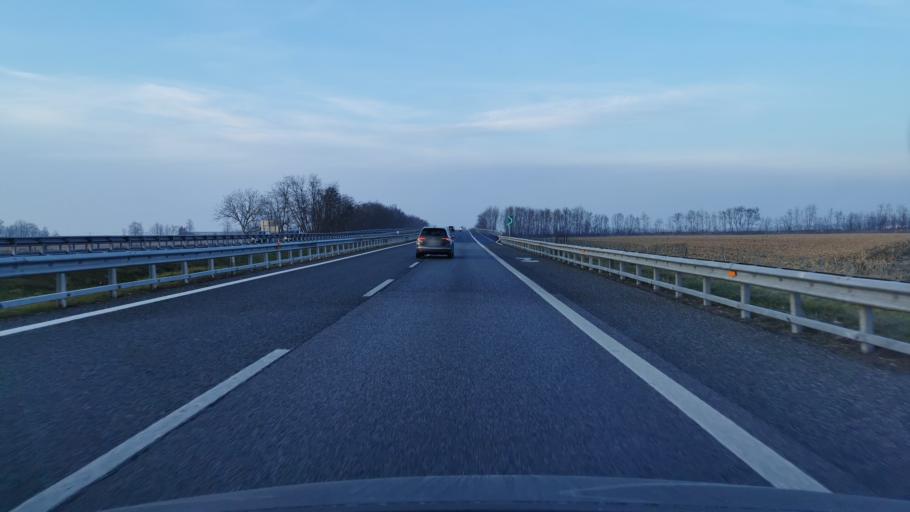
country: IT
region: Piedmont
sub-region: Provincia di Cuneo
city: Caramagna Piemonte
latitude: 44.7940
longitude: 7.7531
